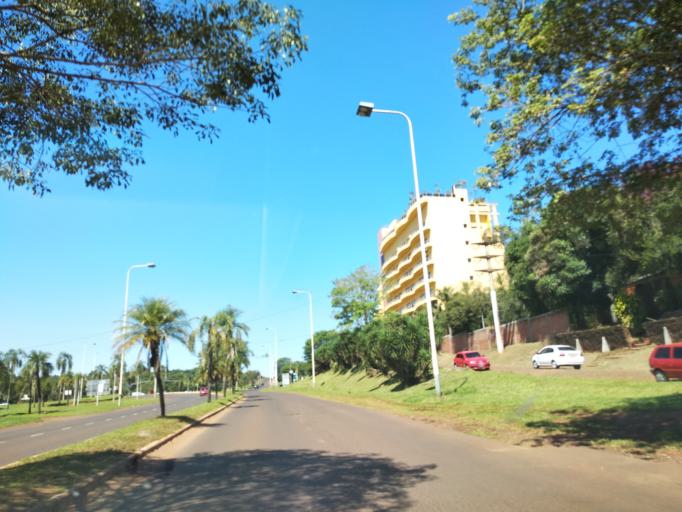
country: AR
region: Misiones
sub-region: Departamento de Iguazu
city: Puerto Iguazu
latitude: -25.6104
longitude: -54.5636
